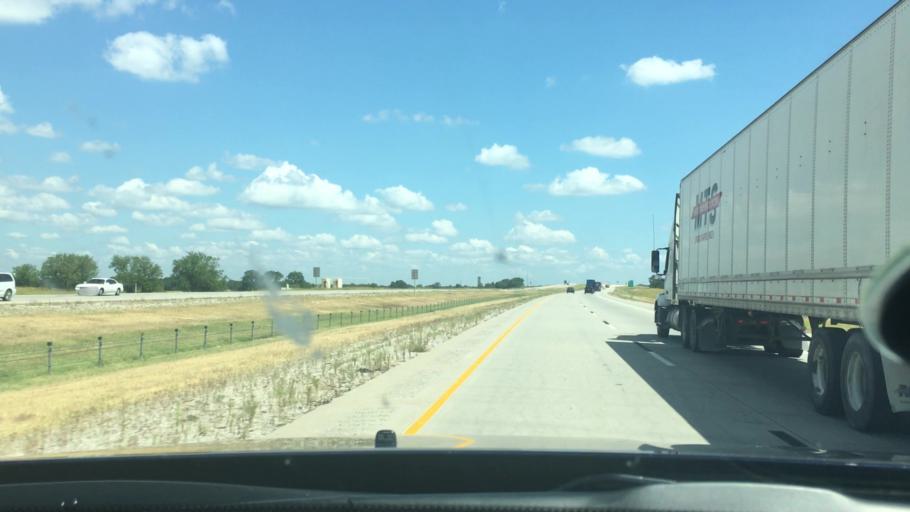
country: US
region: Oklahoma
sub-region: Carter County
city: Ardmore
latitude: 34.1273
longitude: -97.1563
